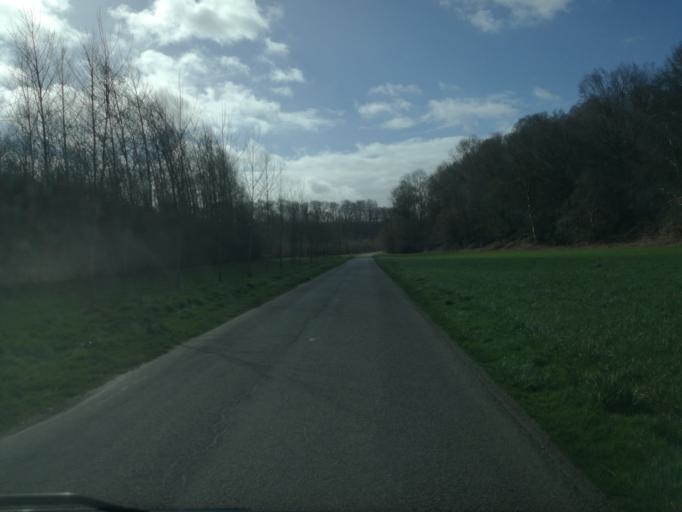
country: FR
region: Haute-Normandie
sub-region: Departement de la Seine-Maritime
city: Yebleron
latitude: 49.6850
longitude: 0.4894
